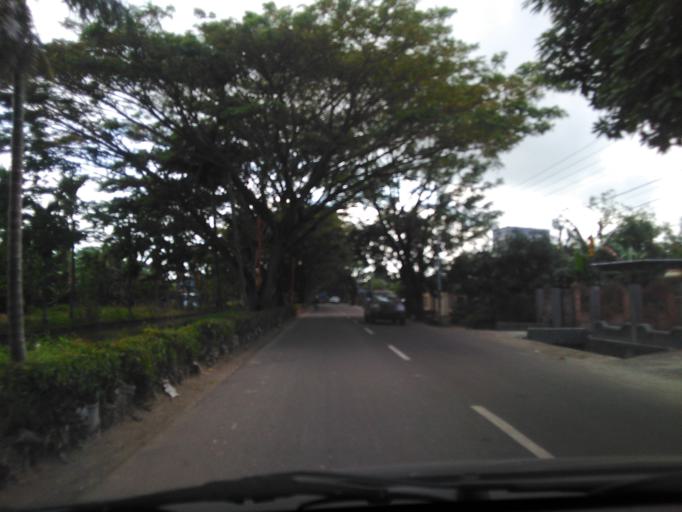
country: ID
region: South Sulawesi
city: Pinrang
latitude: -3.8059
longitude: 119.6457
